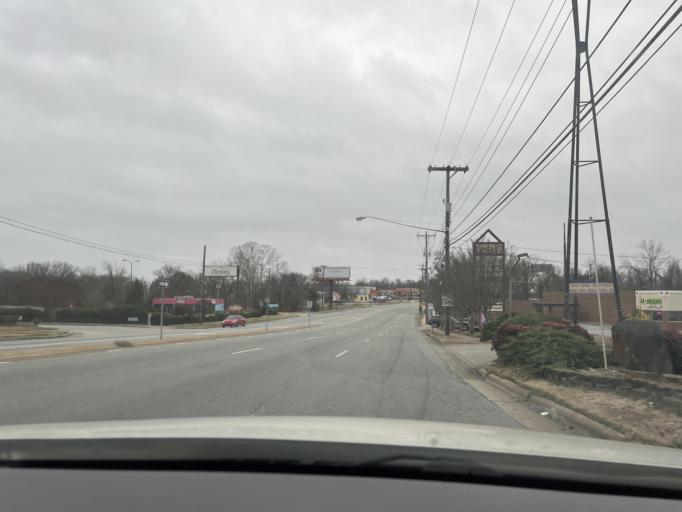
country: US
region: North Carolina
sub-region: Guilford County
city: Greensboro
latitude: 36.0393
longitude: -79.8005
